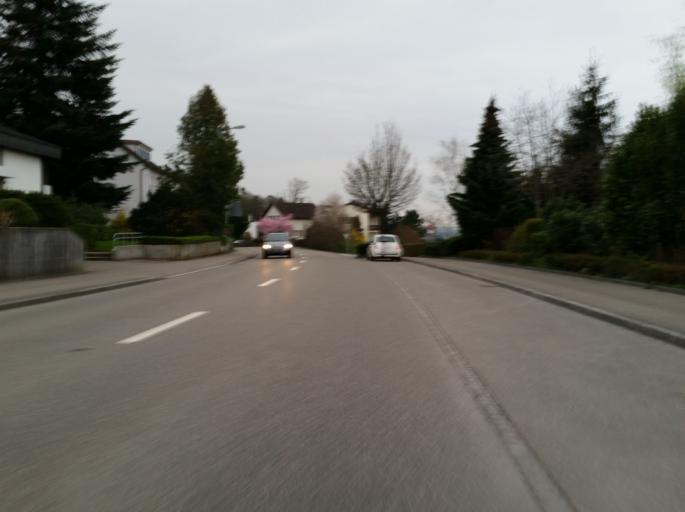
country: CH
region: Appenzell Ausserrhoden
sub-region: Bezirk Vorderland
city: Heiden
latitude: 47.4787
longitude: 9.5376
